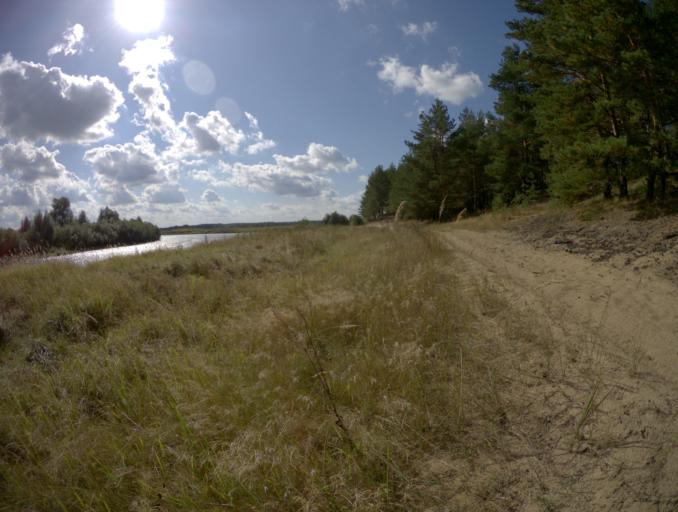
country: RU
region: Moskovskaya
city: Baksheyevo
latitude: 55.8748
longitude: 39.8530
